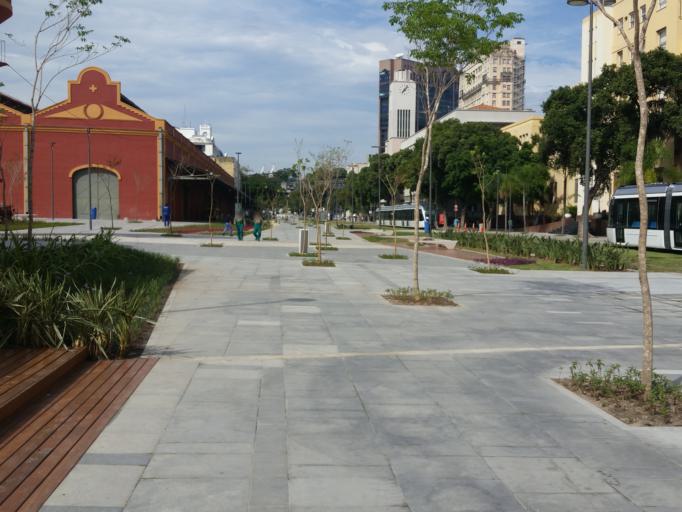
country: BR
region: Rio de Janeiro
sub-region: Rio De Janeiro
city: Rio de Janeiro
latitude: -22.8950
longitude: -43.1845
